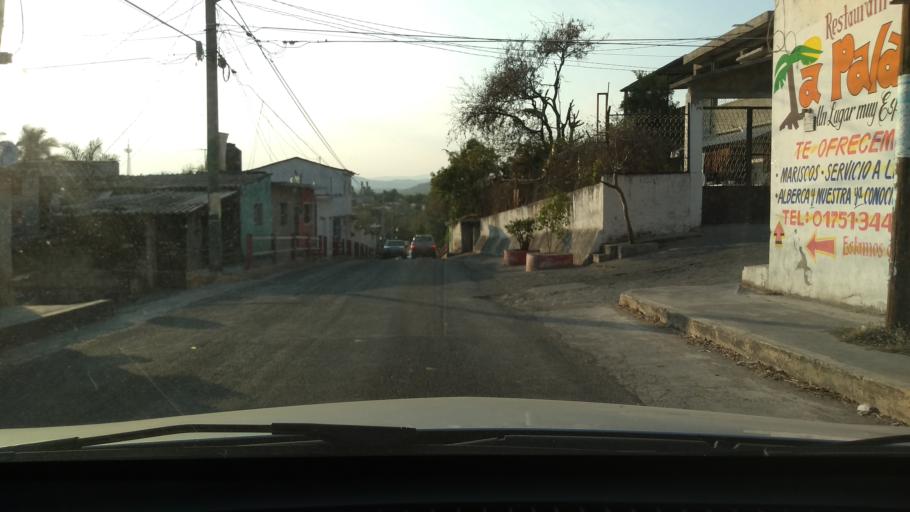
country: MX
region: Morelos
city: Puente de Ixtla
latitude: 18.6204
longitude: -99.3169
